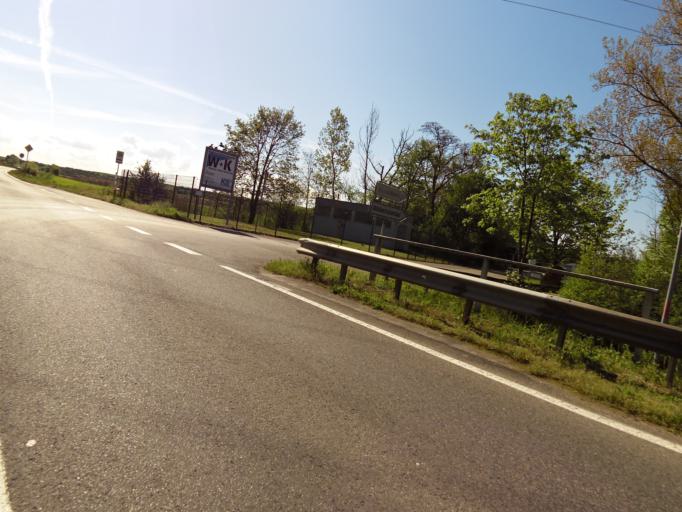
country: DE
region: Rheinland-Pfalz
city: Osthofen
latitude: 49.6713
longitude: 8.3030
